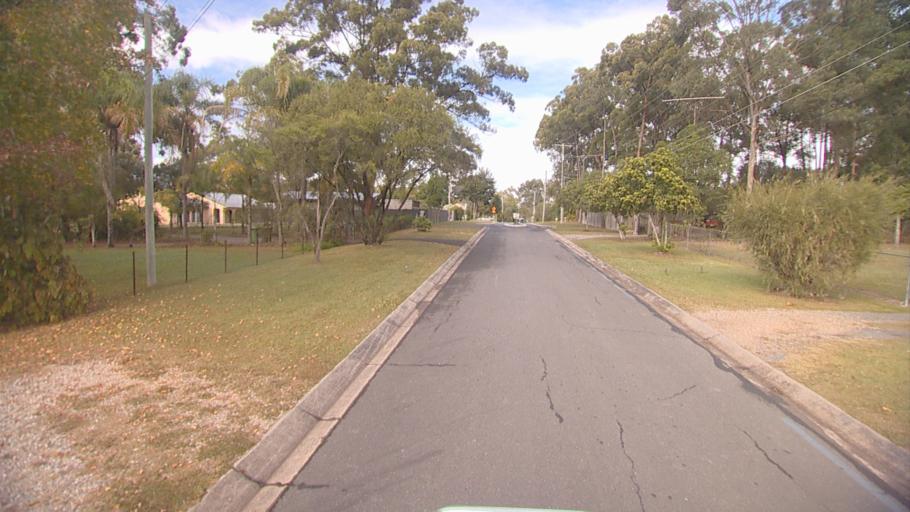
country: AU
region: Queensland
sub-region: Logan
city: Waterford West
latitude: -27.6841
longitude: 153.1245
